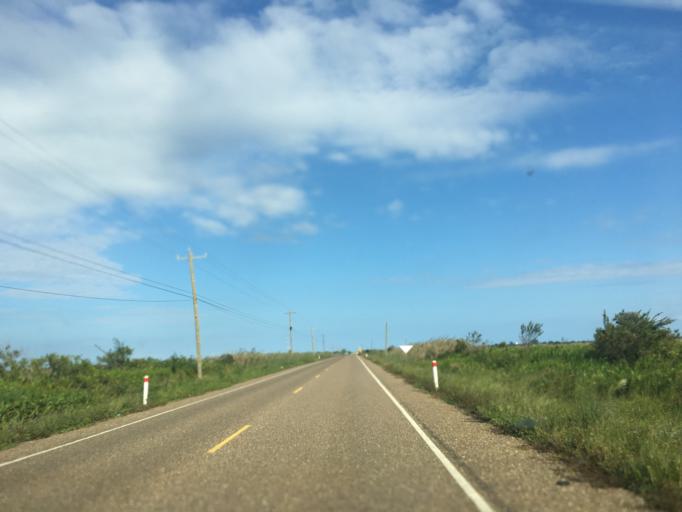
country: BZ
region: Stann Creek
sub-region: Dangriga
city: Dangriga
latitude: 16.8581
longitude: -88.3030
